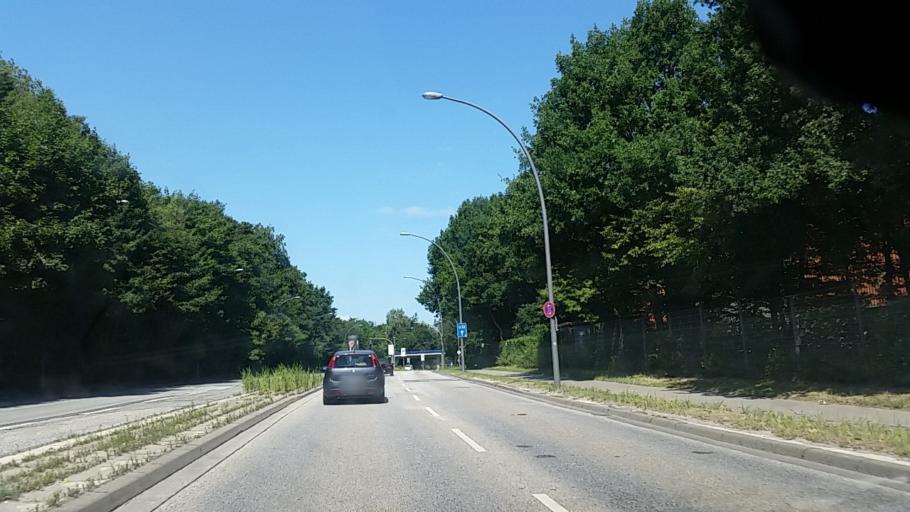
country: DE
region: Hamburg
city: Stellingen
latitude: 53.5843
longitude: 9.9097
